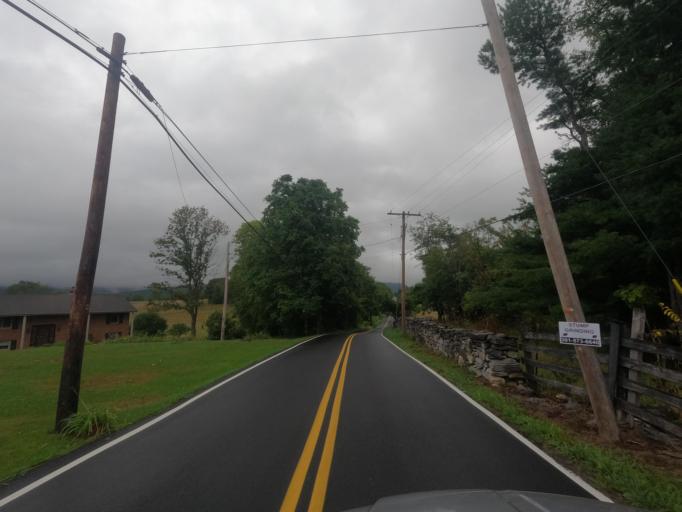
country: US
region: Maryland
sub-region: Washington County
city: Wilson-Conococheague
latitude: 39.6437
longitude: -77.9295
